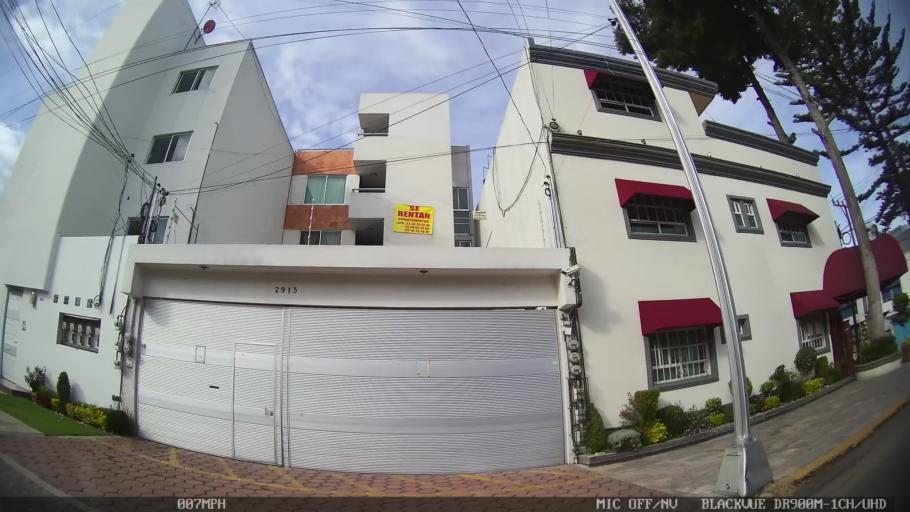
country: MX
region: Puebla
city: Puebla
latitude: 19.0508
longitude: -98.2230
